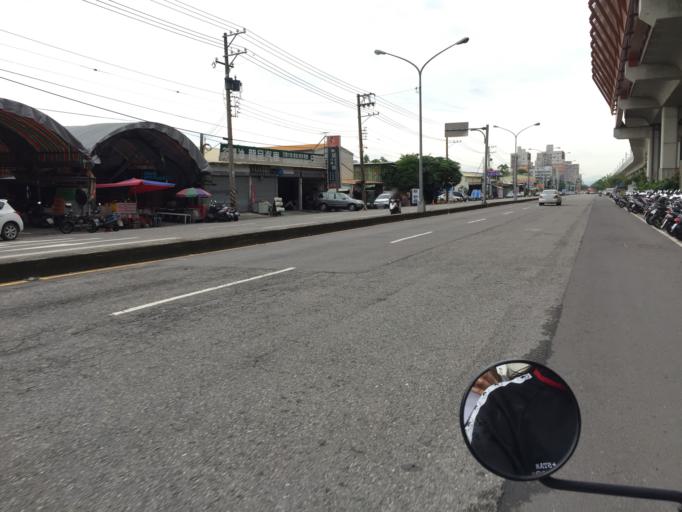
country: TW
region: Taiwan
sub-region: Taichung City
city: Taichung
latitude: 24.1647
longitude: 120.6996
